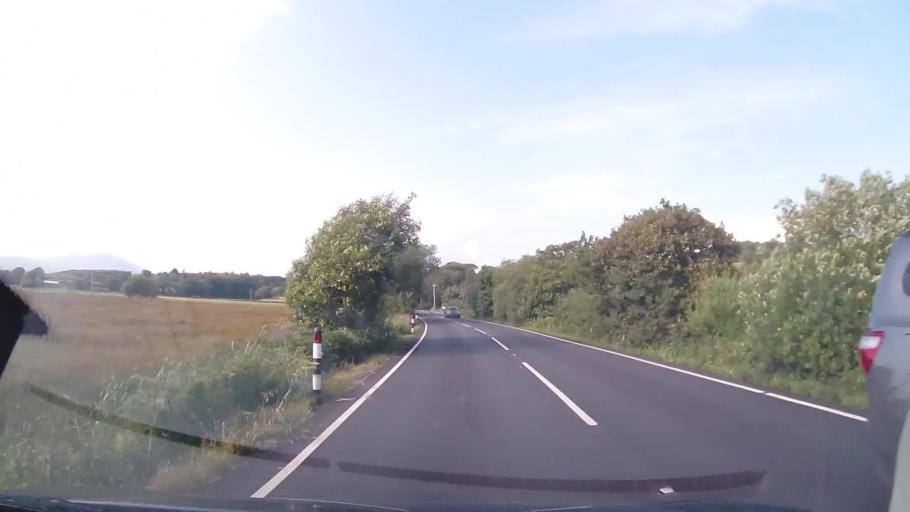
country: GB
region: Wales
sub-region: Gwynedd
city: Penrhyndeudraeth
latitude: 52.9123
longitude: -4.0527
